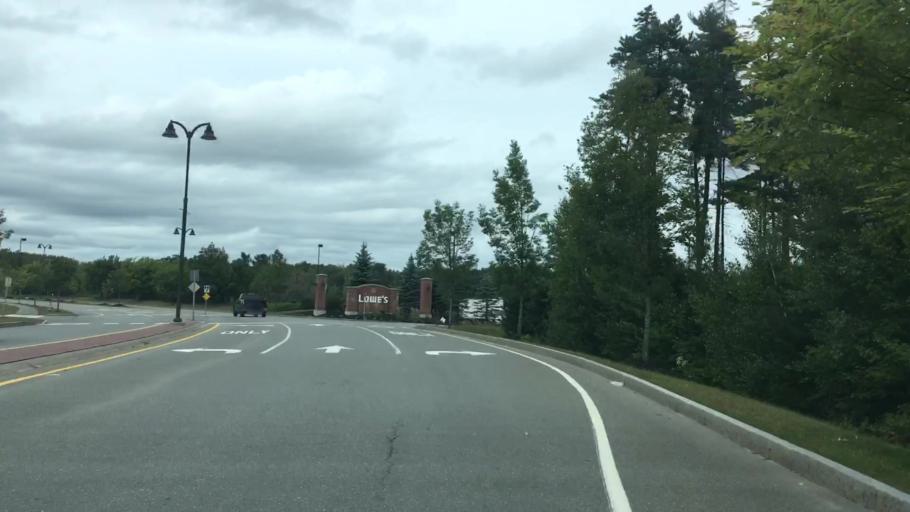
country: US
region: Maine
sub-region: Cumberland County
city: South Portland Gardens
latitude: 43.6224
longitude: -70.3392
